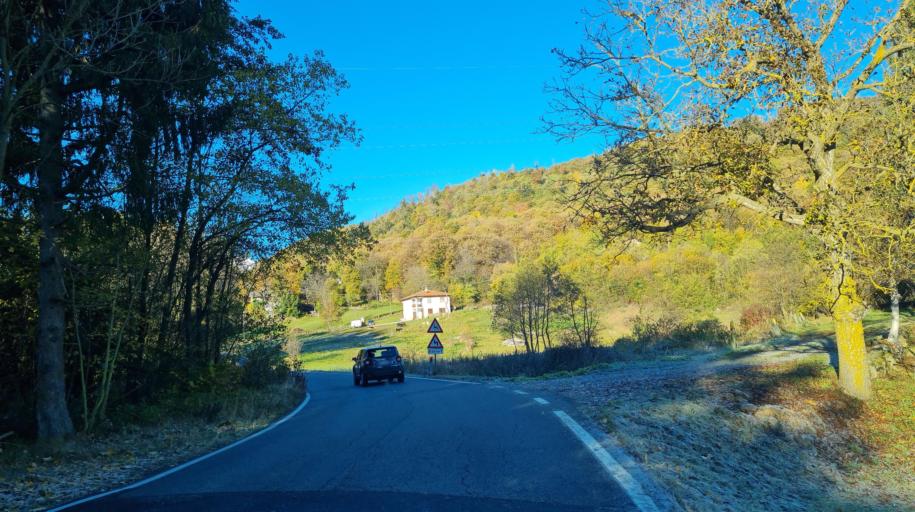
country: IT
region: Piedmont
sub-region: Provincia di Torino
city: Alice Superiore
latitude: 45.4608
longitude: 7.7901
